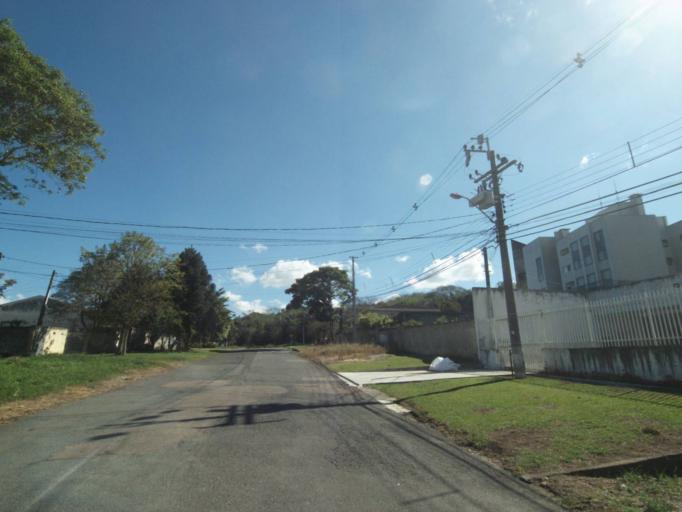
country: BR
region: Parana
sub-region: Curitiba
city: Curitiba
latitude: -25.4015
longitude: -49.2522
